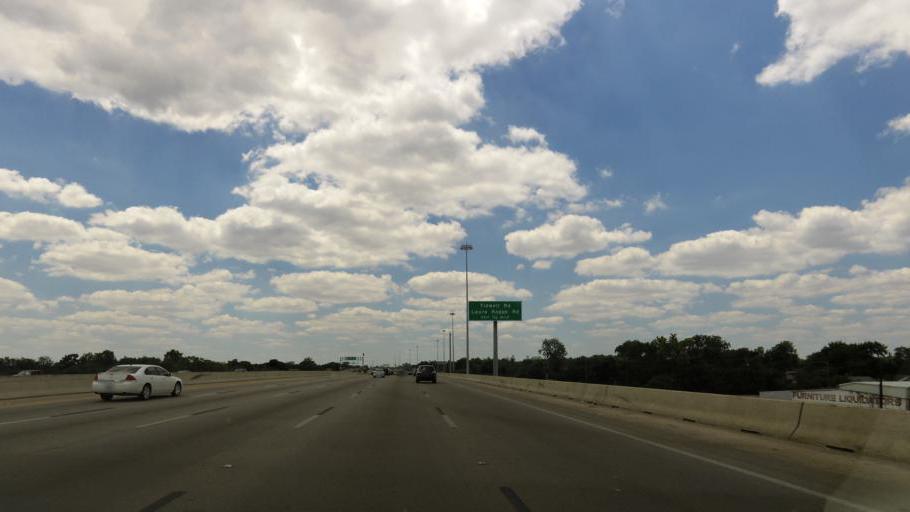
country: US
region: Texas
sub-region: Harris County
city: Aldine
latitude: 29.8606
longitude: -95.3338
